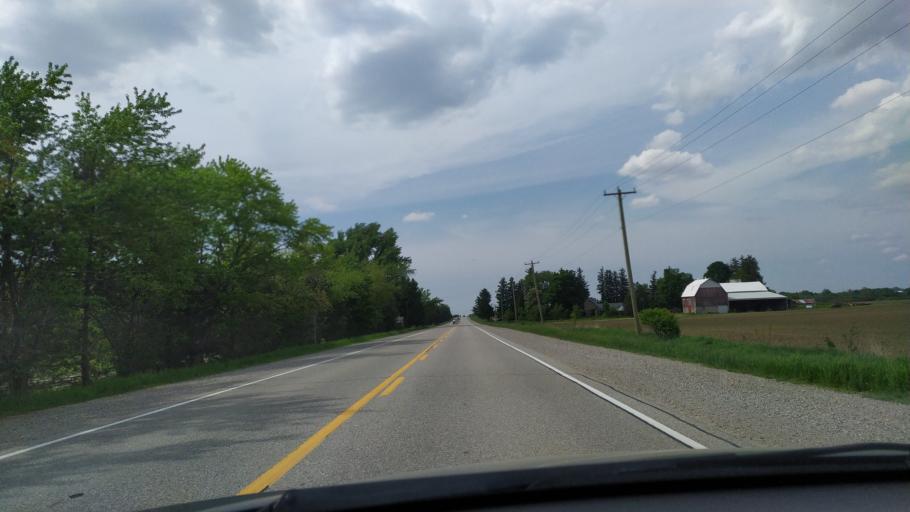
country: CA
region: Ontario
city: Stratford
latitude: 43.2029
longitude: -81.0625
